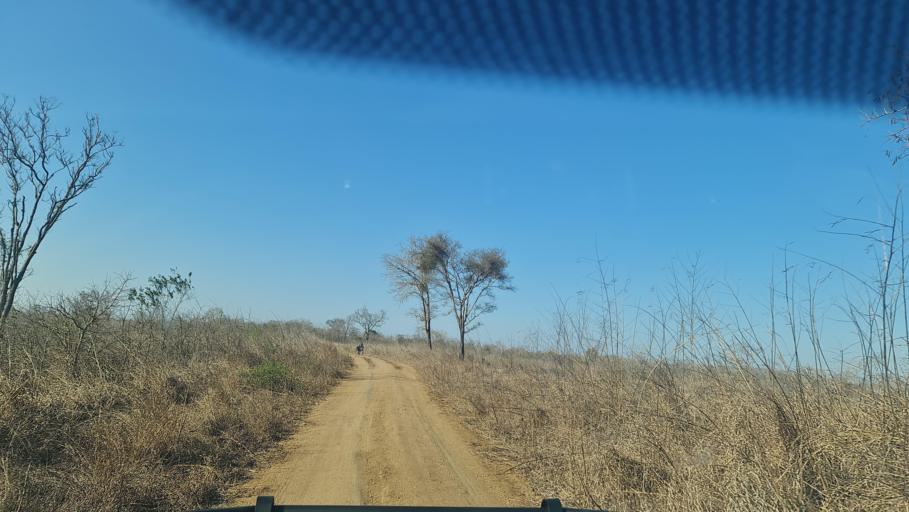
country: MZ
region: Nampula
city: Nacala
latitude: -13.9487
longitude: 40.4784
